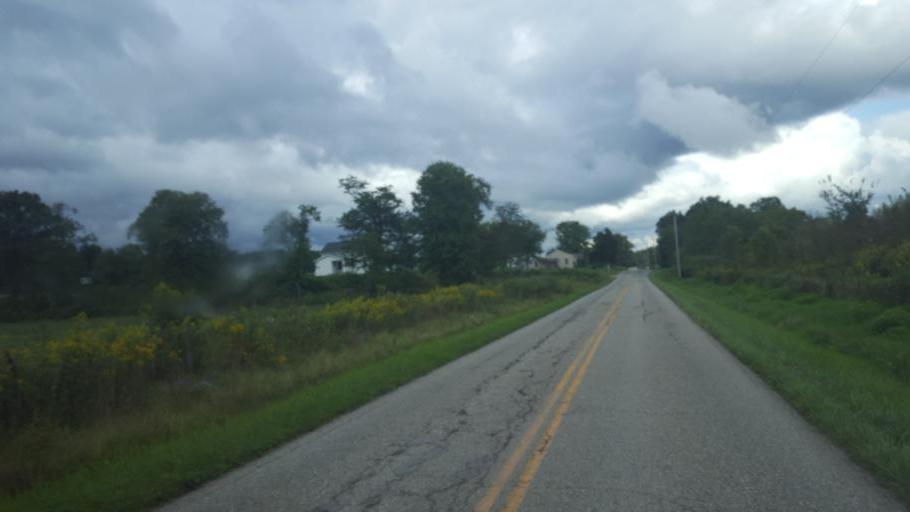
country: US
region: Ohio
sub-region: Jackson County
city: Oak Hill
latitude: 38.9358
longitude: -82.5738
